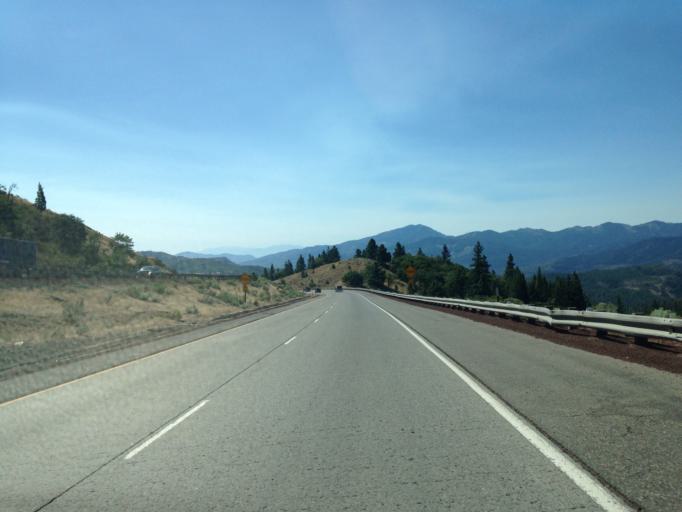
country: US
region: Oregon
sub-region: Jackson County
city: Ashland
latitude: 42.0556
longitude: -122.6102
